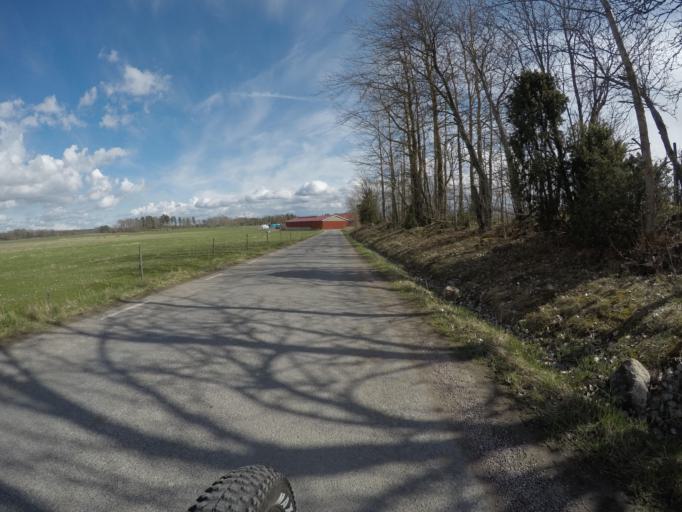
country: SE
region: Vaestmanland
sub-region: Kungsors Kommun
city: Kungsoer
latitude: 59.2992
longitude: 16.1393
